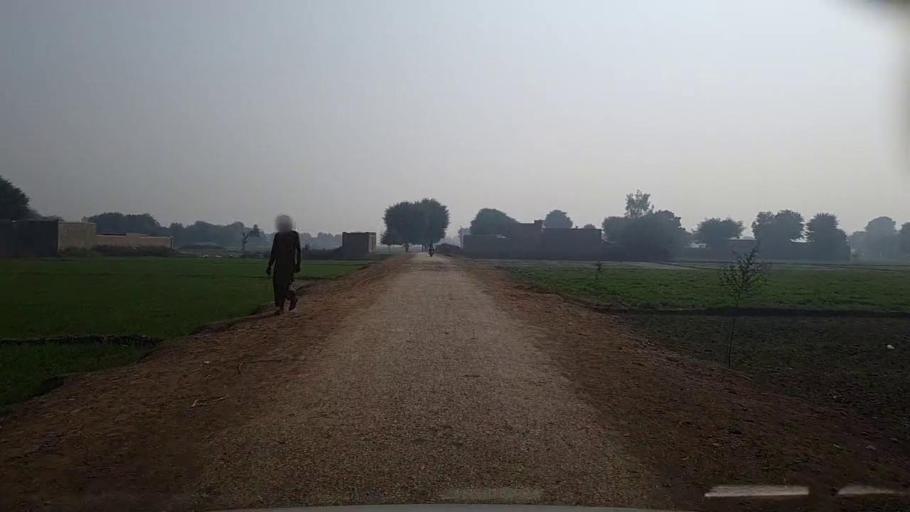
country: PK
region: Sindh
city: Setharja Old
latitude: 27.1526
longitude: 68.4652
